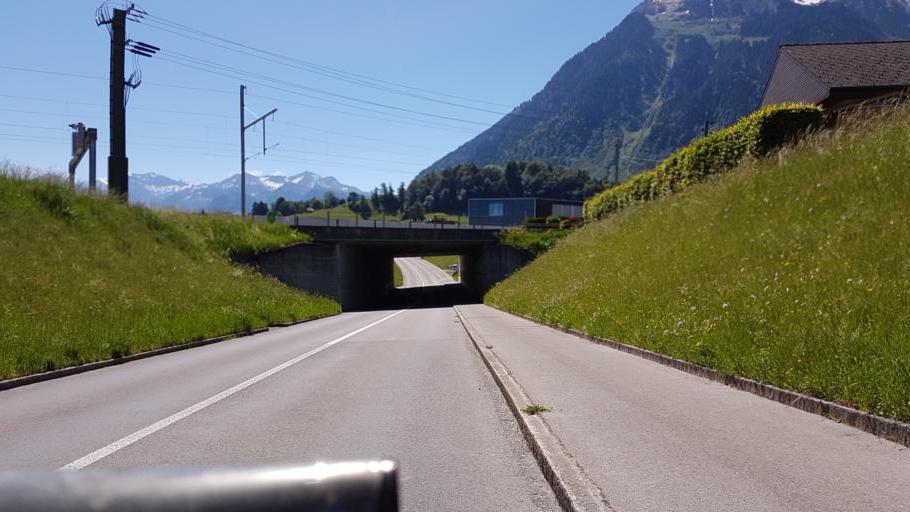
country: CH
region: Bern
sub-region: Frutigen-Niedersimmental District
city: Wimmis
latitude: 46.6825
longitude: 7.6402
